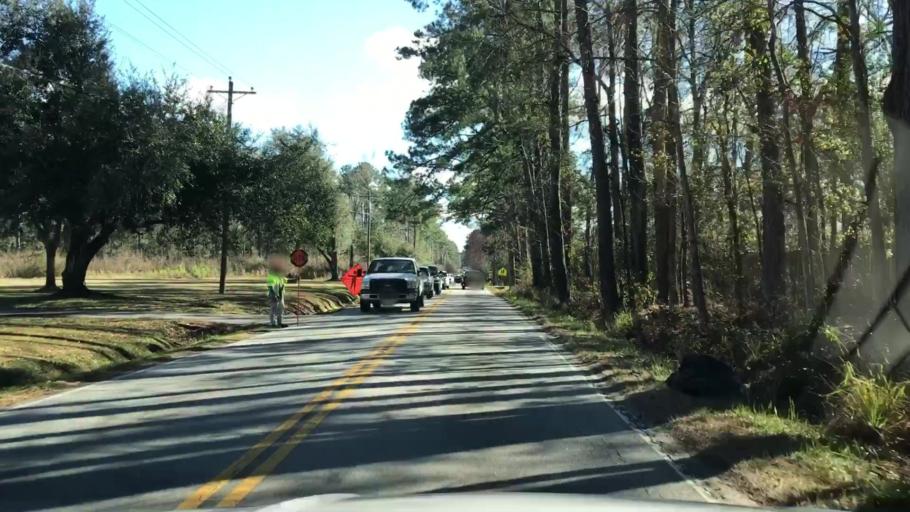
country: US
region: South Carolina
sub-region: Dorchester County
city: Summerville
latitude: 33.0325
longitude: -80.2458
